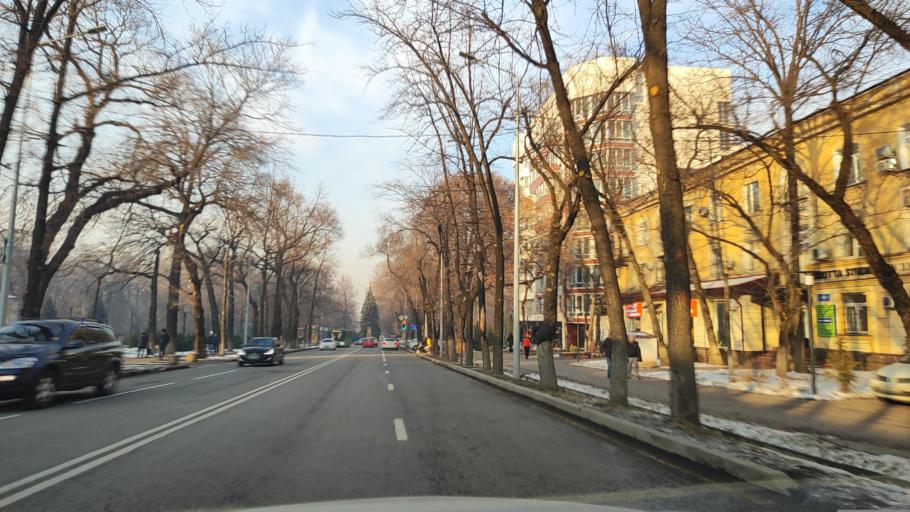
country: KZ
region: Almaty Qalasy
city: Almaty
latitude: 43.2561
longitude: 76.9553
